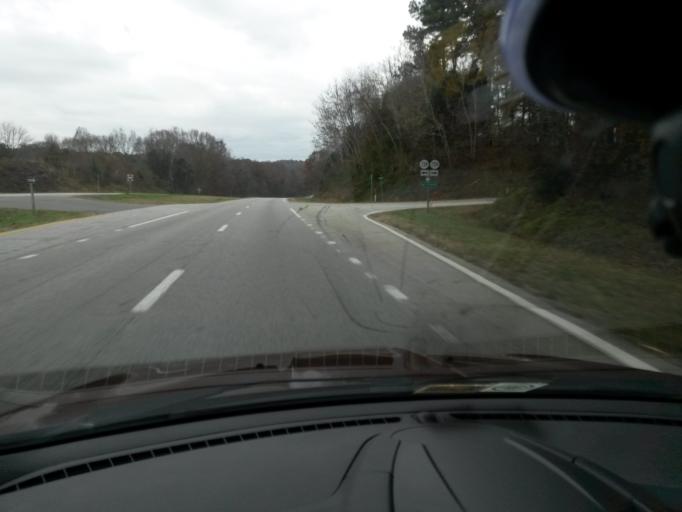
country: US
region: Virginia
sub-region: Amherst County
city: Amherst
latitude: 37.6626
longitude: -78.9553
